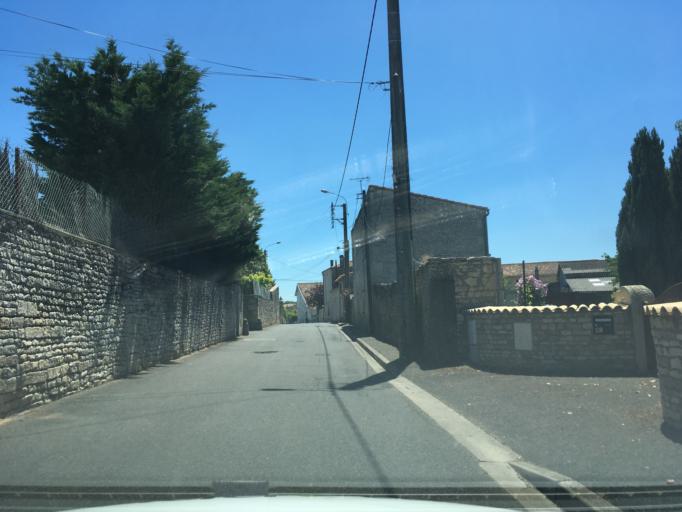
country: FR
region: Poitou-Charentes
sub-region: Departement des Deux-Sevres
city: Niort
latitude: 46.3298
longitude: -0.4265
